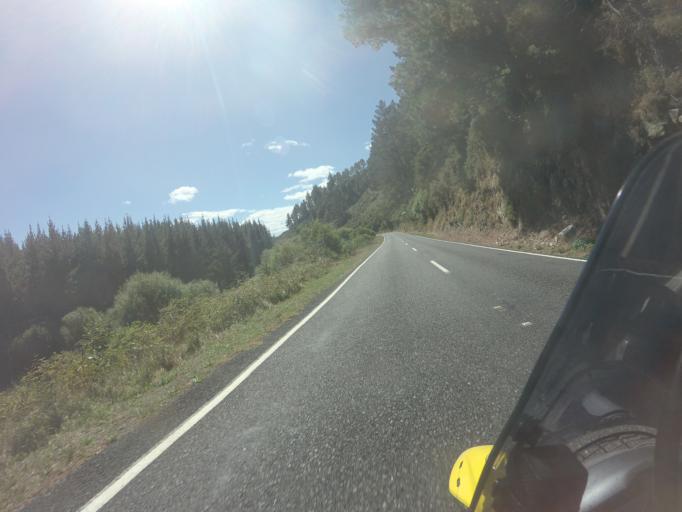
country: NZ
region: Bay of Plenty
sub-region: Kawerau District
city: Kawerau
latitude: -38.2683
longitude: 176.8197
